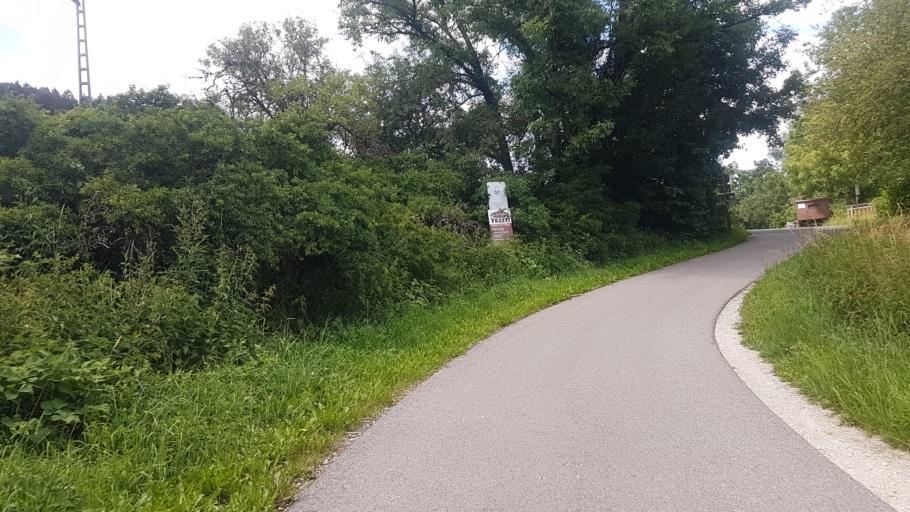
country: DE
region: Bavaria
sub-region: Regierungsbezirk Mittelfranken
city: Solnhofen
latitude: 48.8871
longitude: 11.0177
